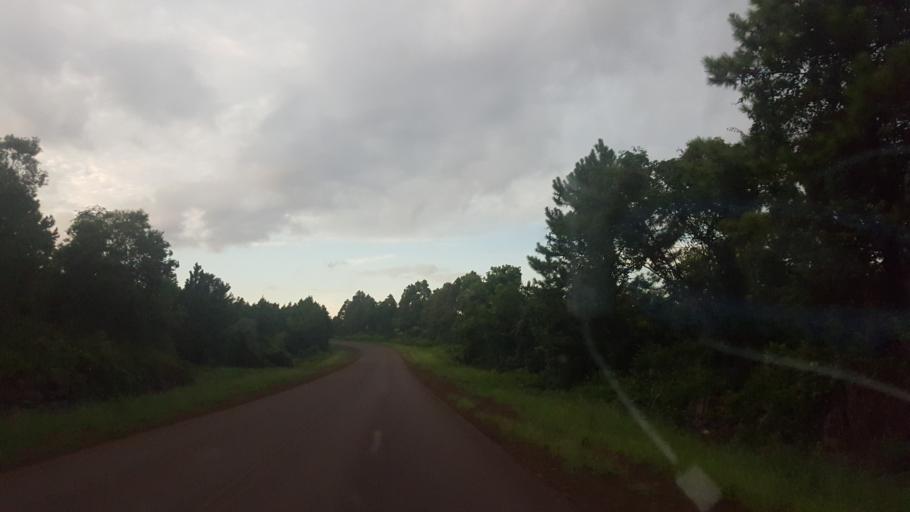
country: AR
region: Misiones
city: Dos de Mayo
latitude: -26.9482
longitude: -54.7147
